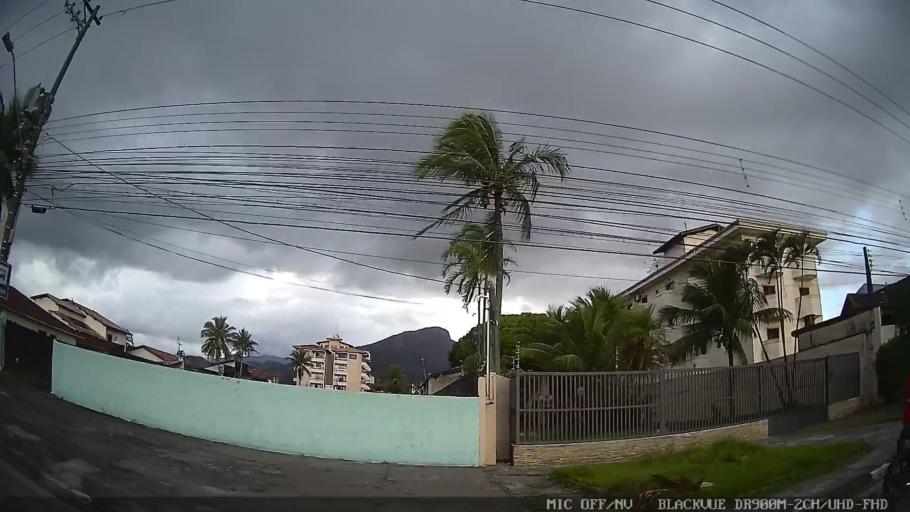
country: BR
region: Sao Paulo
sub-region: Caraguatatuba
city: Caraguatatuba
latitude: -23.6338
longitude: -45.4191
